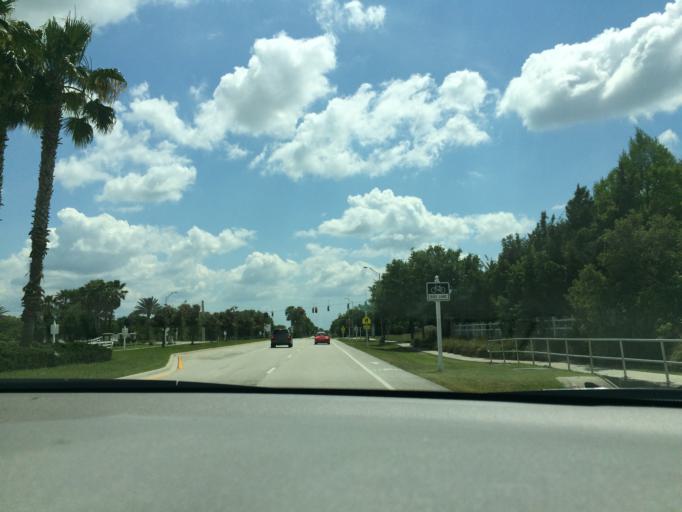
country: US
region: Florida
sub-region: Sarasota County
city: The Meadows
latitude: 27.3971
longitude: -82.3984
